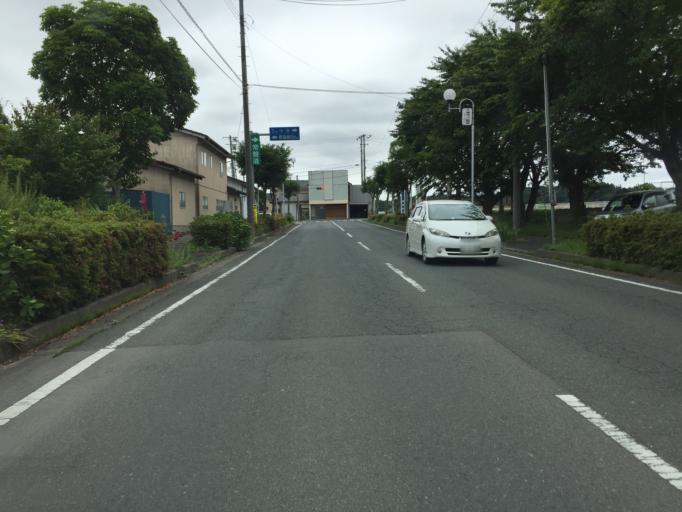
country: JP
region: Fukushima
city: Namie
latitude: 37.7019
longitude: 140.9653
